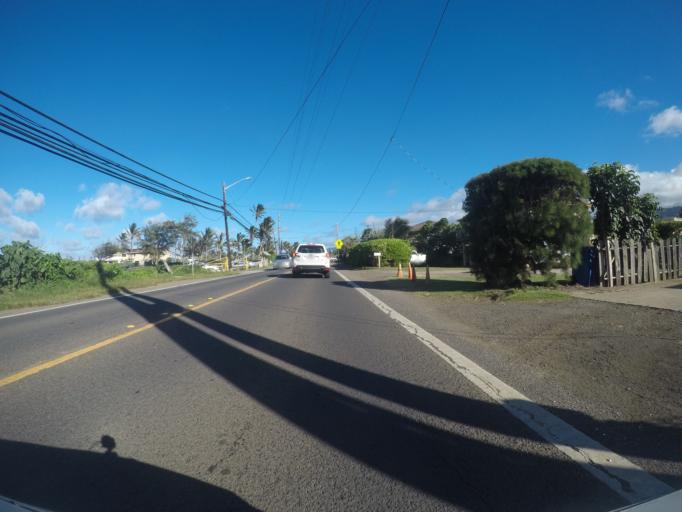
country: US
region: Hawaii
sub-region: Honolulu County
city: La'ie
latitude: 21.6530
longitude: -157.9292
